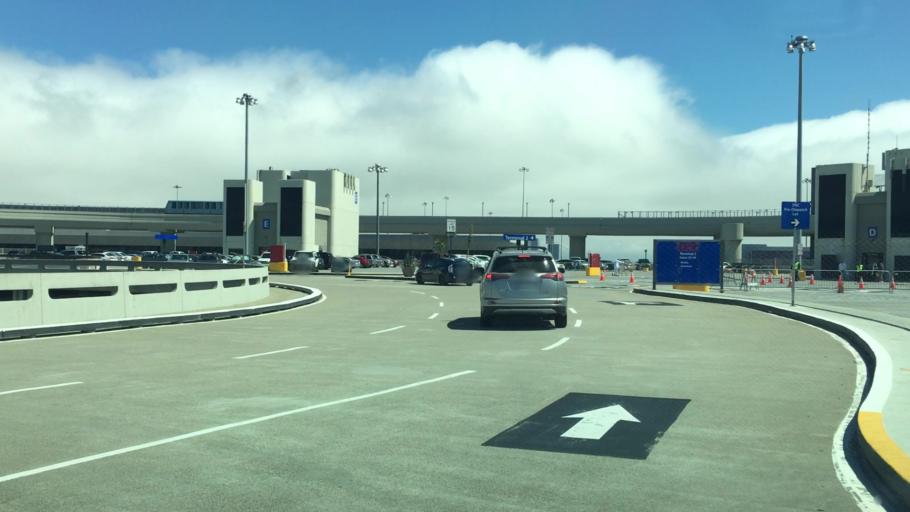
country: US
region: California
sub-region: San Mateo County
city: Millbrae
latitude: 37.6160
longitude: -122.3859
